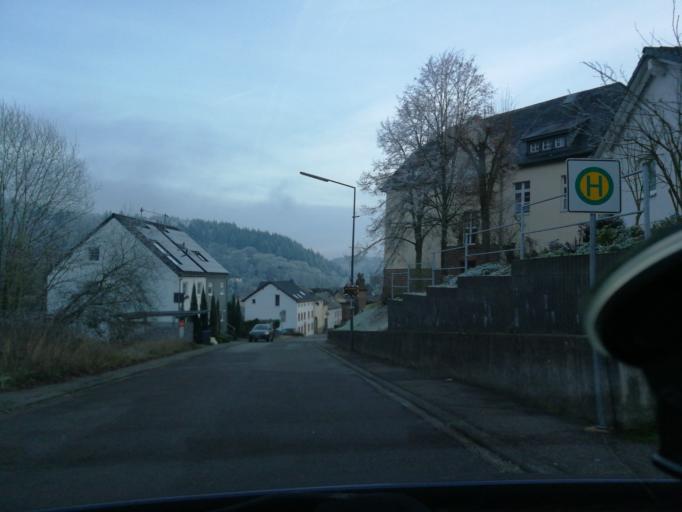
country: DE
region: Rheinland-Pfalz
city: Aach
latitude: 49.7906
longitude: 6.5888
